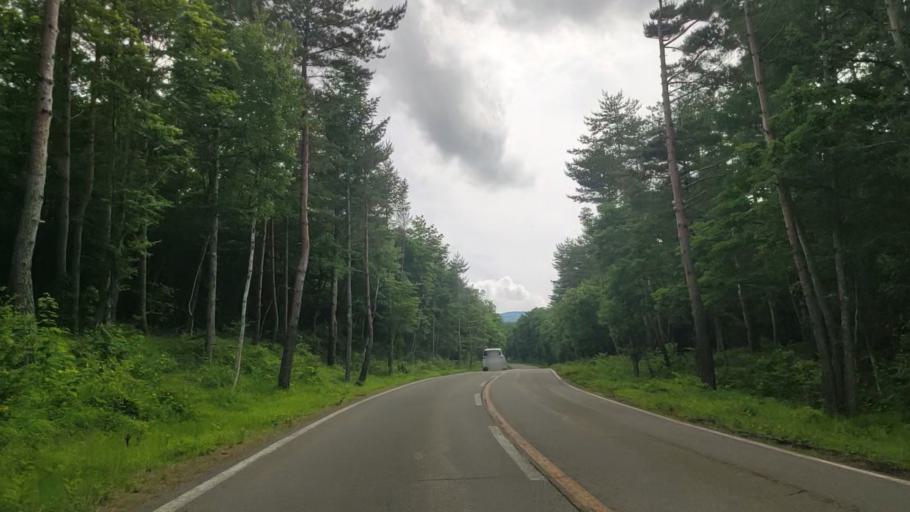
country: JP
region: Yamanashi
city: Fujikawaguchiko
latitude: 35.4359
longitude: 138.7406
